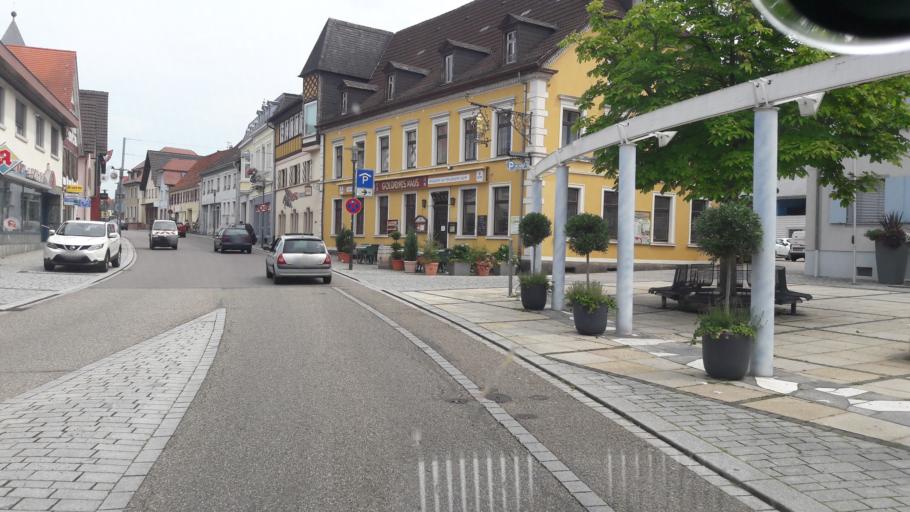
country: DE
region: Baden-Wuerttemberg
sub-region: Freiburg Region
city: Renchen
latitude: 48.5862
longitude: 8.0116
